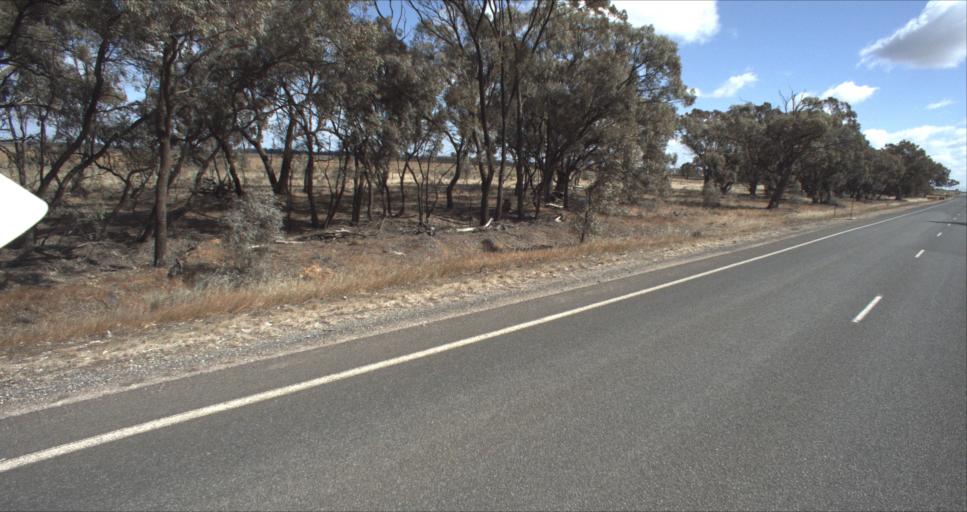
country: AU
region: New South Wales
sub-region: Murrumbidgee Shire
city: Darlington Point
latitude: -34.5572
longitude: 146.1697
